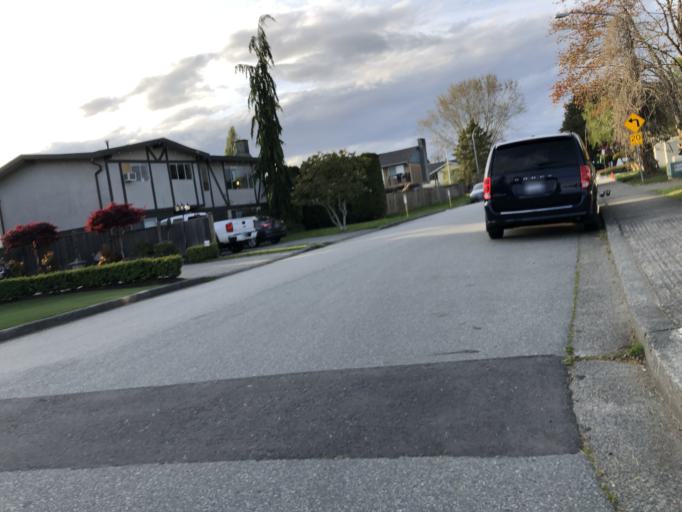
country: CA
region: British Columbia
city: Richmond
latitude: 49.1440
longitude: -123.1090
